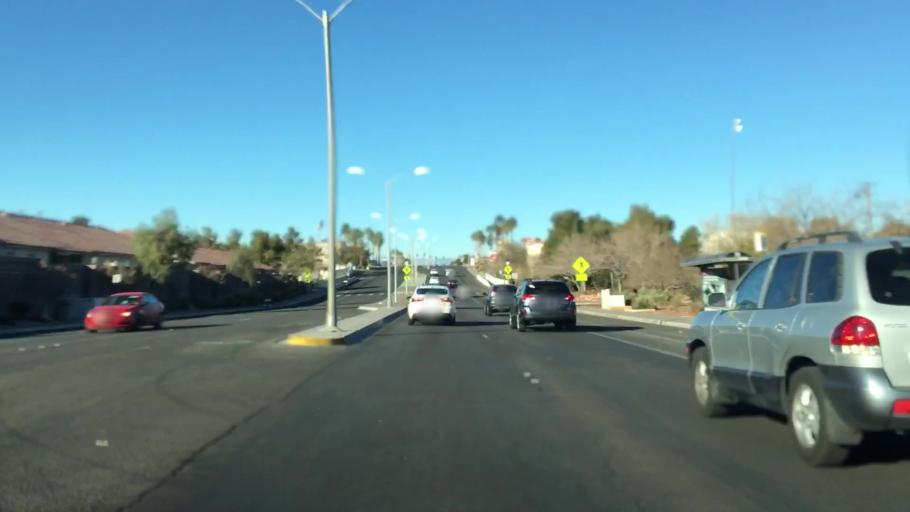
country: US
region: Nevada
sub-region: Clark County
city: Whitney
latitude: 36.0384
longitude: -115.1001
